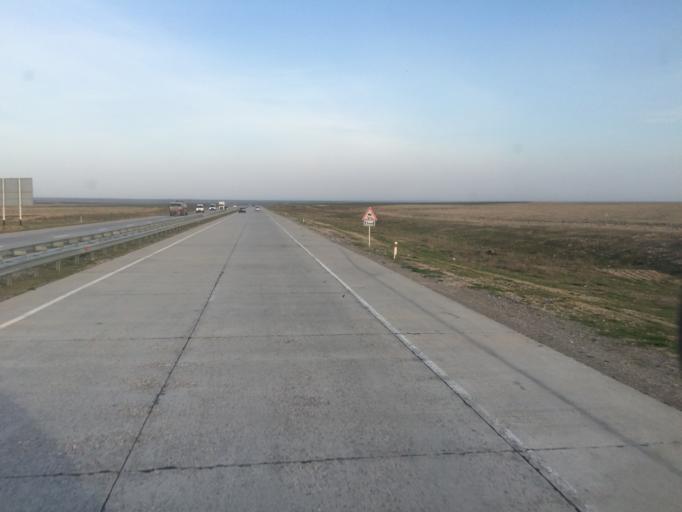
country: KZ
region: Ongtustik Qazaqstan
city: Temirlanovka
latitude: 42.6472
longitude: 69.2438
